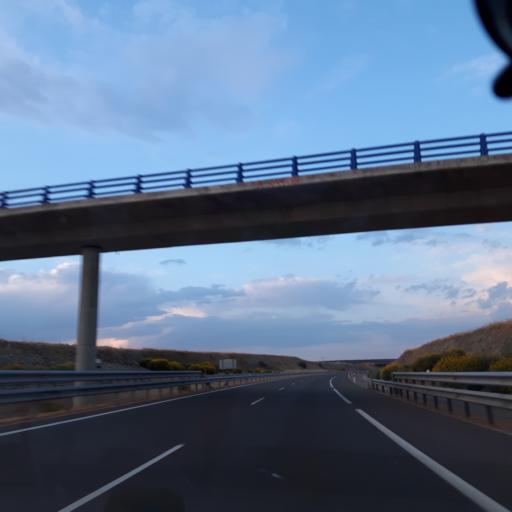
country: ES
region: Castille and Leon
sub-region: Provincia de Salamanca
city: Mozarbez
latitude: 40.8607
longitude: -5.6430
